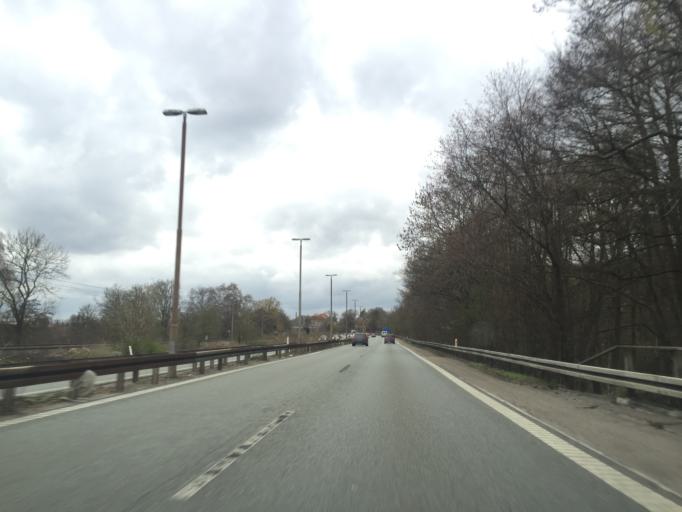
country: DK
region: Capital Region
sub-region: Lyngby-Tarbaek Kommune
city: Kongens Lyngby
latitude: 55.7750
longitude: 12.4934
